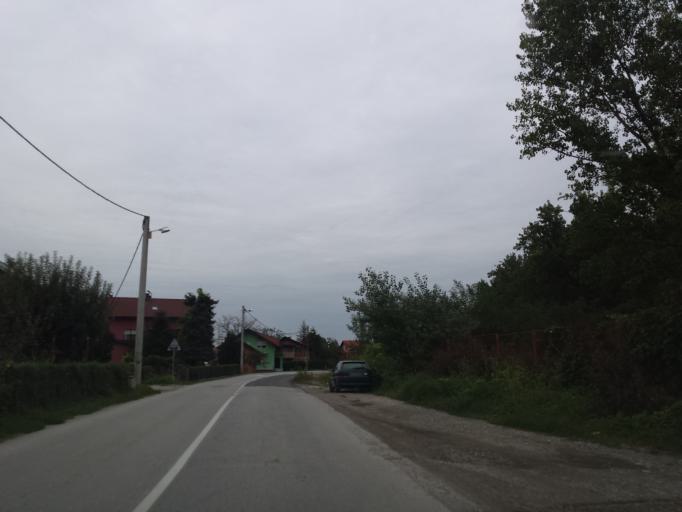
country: HR
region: Grad Zagreb
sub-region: Sesvete
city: Sesvete
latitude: 45.7906
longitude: 16.1369
